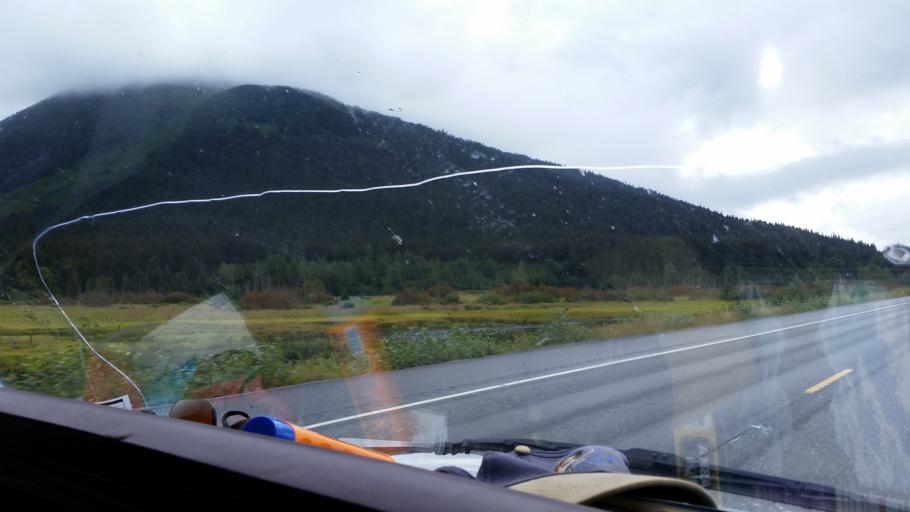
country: US
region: Alaska
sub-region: Anchorage Municipality
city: Girdwood
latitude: 60.9348
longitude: -149.1578
